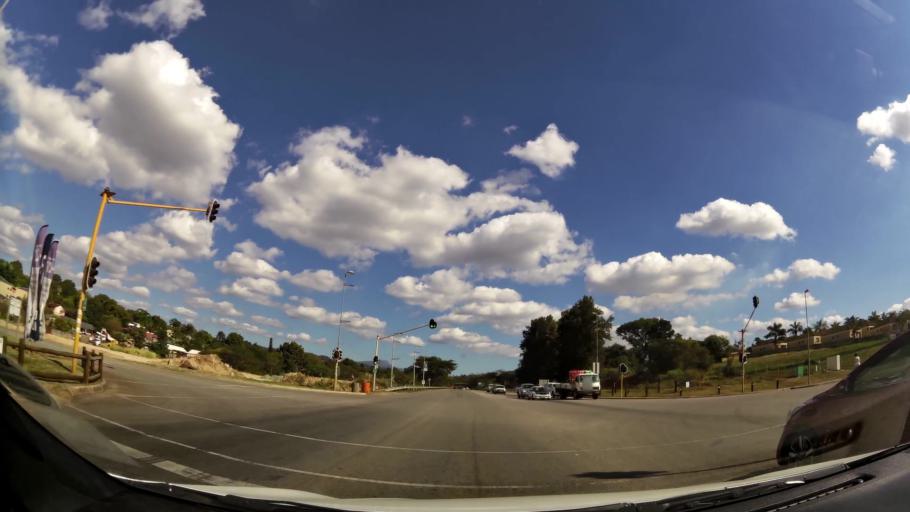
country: ZA
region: Limpopo
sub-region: Mopani District Municipality
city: Tzaneen
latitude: -23.8251
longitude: 30.1554
